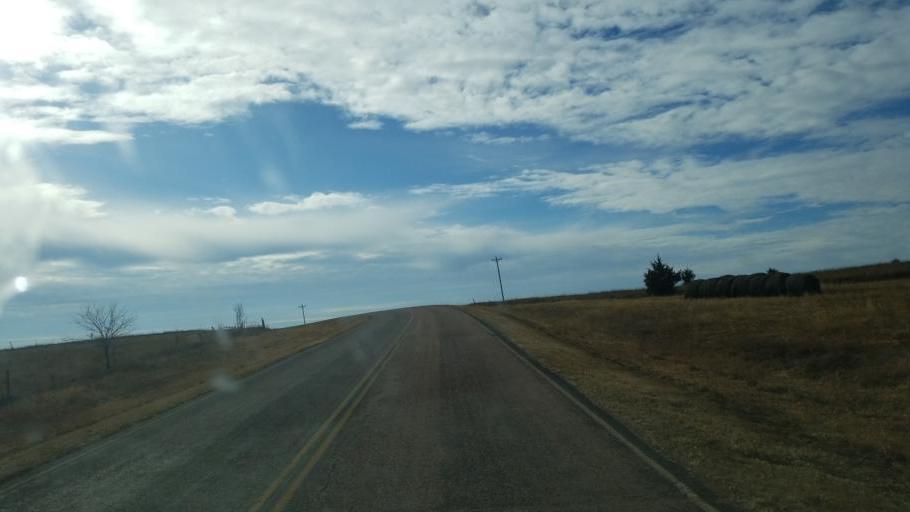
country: US
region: South Dakota
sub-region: Charles Mix County
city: Wagner
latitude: 42.9723
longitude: -98.1874
